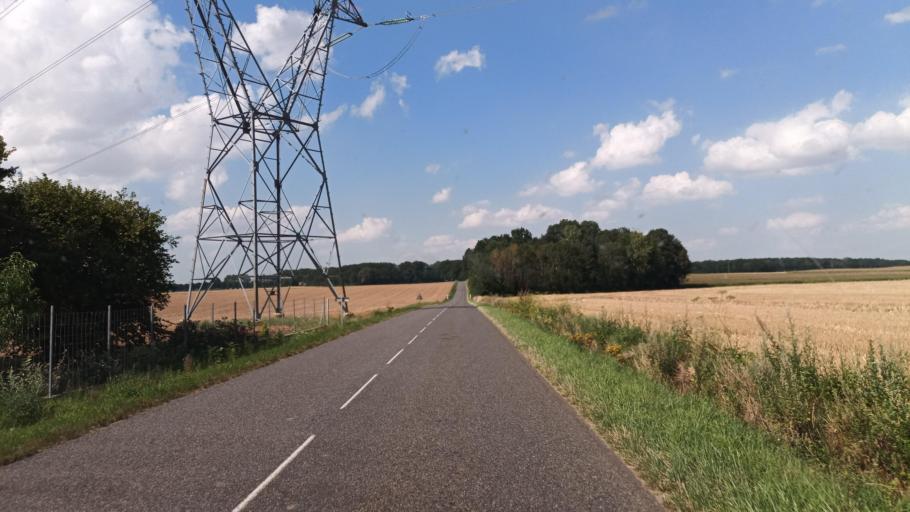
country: FR
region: Bourgogne
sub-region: Departement de l'Yonne
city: Saint-Valerien
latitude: 48.1649
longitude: 3.0997
